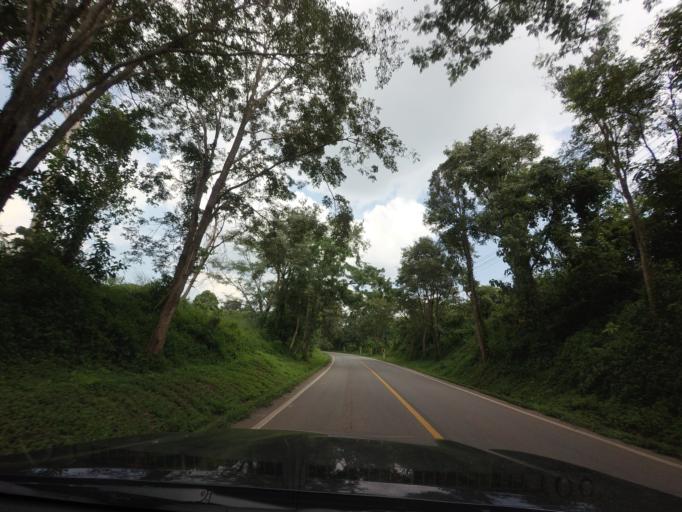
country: TH
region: Uttaradit
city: Ban Khok
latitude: 18.0534
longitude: 101.1118
